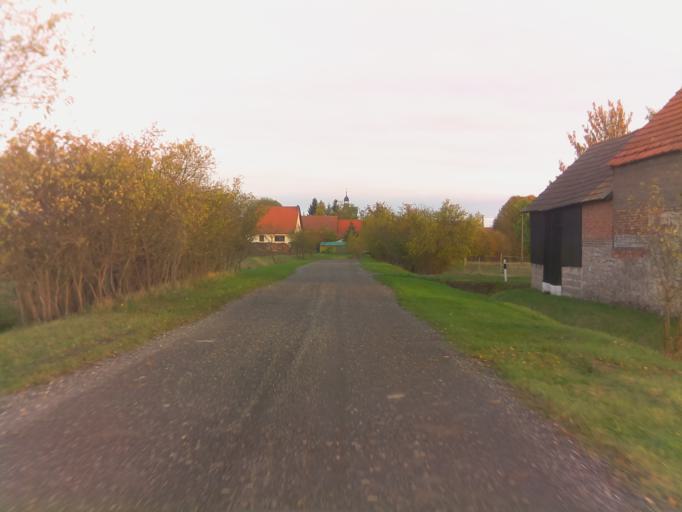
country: DE
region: Thuringia
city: Blankenhain
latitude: 50.8410
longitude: 11.3969
